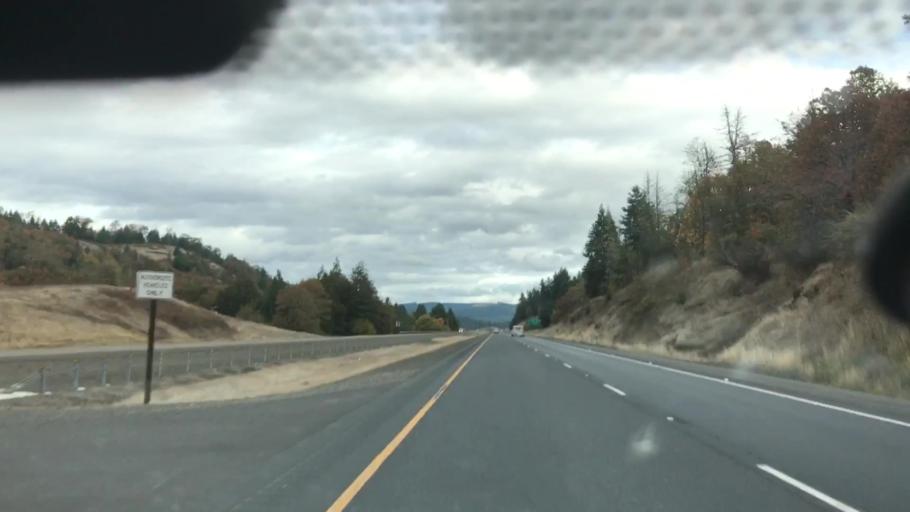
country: US
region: Oregon
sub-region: Douglas County
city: Yoncalla
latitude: 43.5959
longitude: -123.2415
